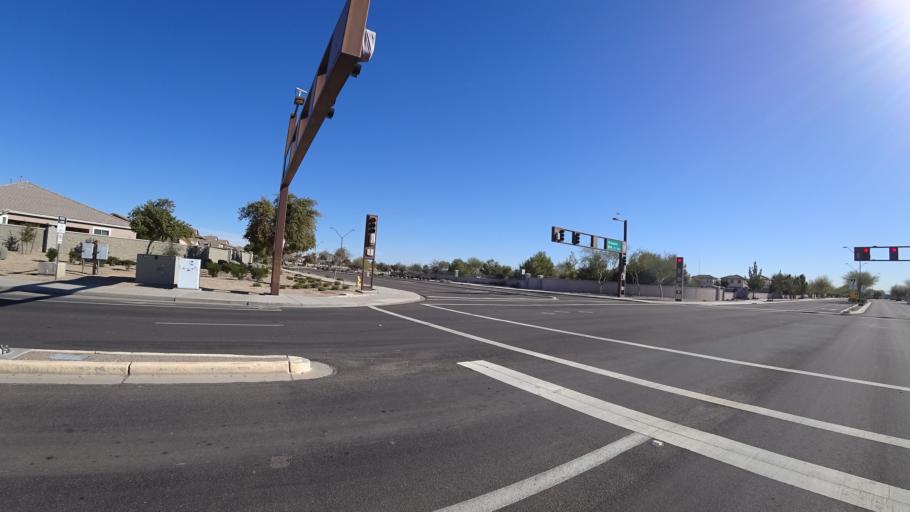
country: US
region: Arizona
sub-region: Maricopa County
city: Litchfield Park
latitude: 33.4742
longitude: -112.3833
